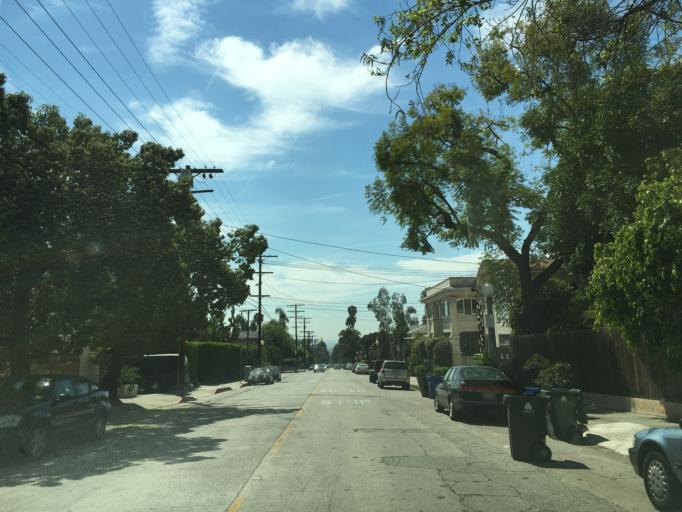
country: US
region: California
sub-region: Los Angeles County
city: Hollywood
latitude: 34.1171
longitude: -118.3215
